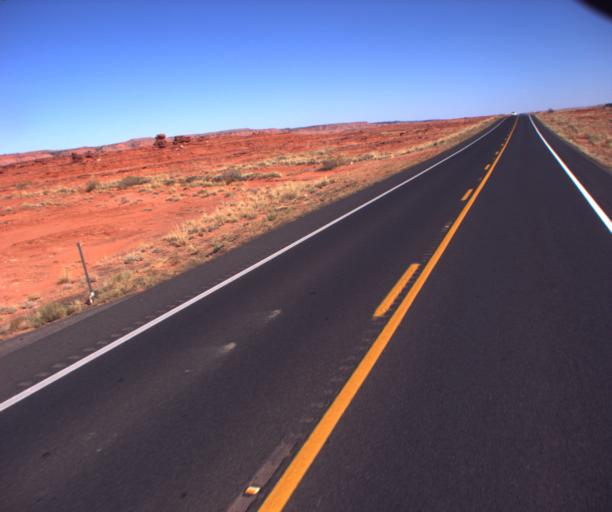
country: US
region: Arizona
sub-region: Coconino County
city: Tuba City
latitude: 36.0990
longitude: -111.3382
